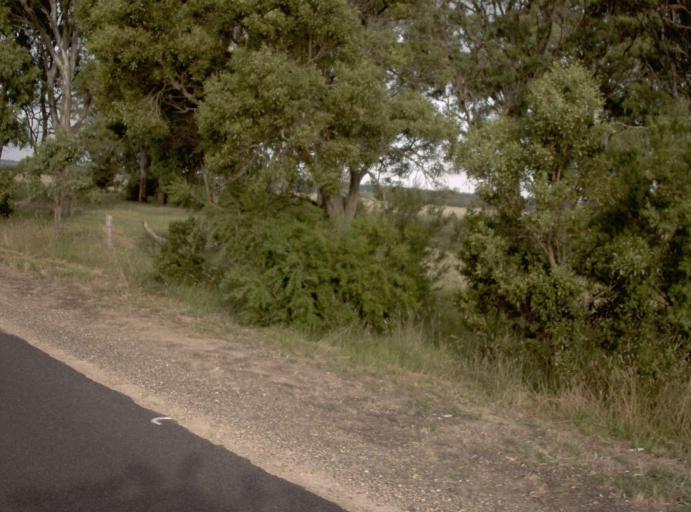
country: AU
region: Victoria
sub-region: Wellington
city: Sale
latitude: -37.8582
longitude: 147.0400
